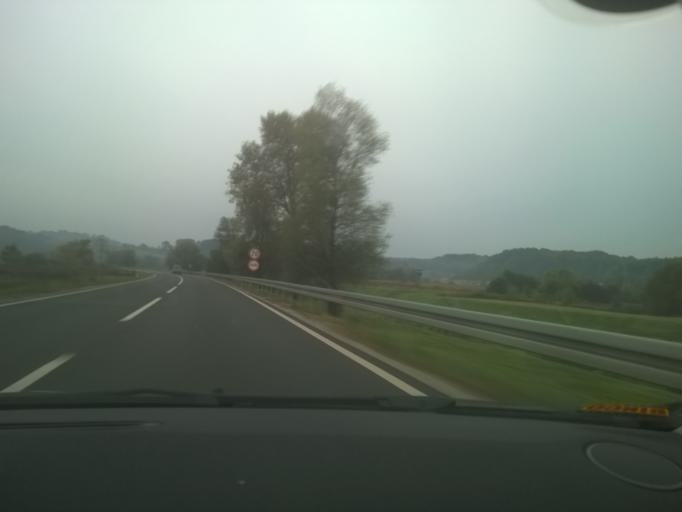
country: HR
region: Zagrebacka
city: Jakovlje
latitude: 45.9880
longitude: 15.8484
